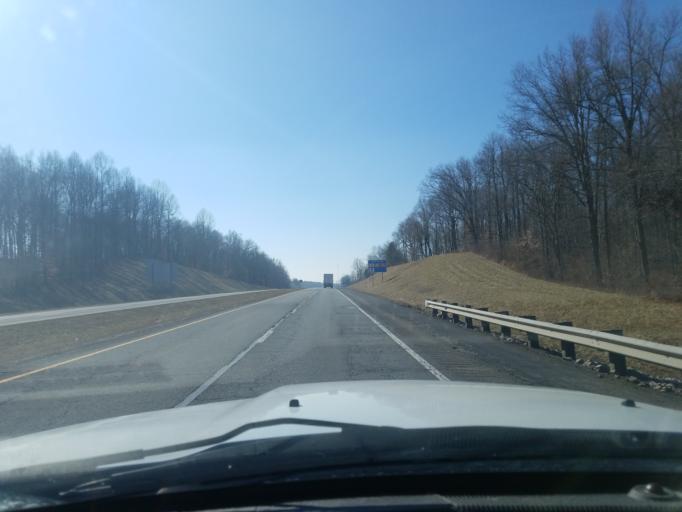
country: US
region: Kentucky
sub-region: Hardin County
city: Elizabethtown
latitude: 37.6649
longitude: -85.8809
